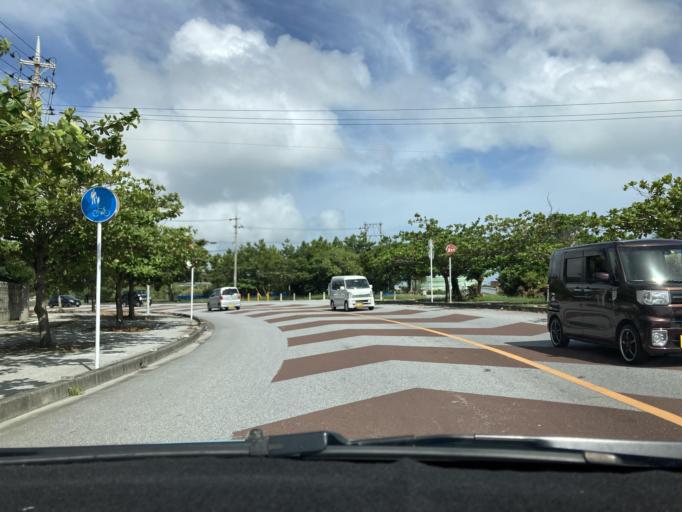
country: JP
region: Okinawa
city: Ginowan
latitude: 26.2189
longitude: 127.7773
